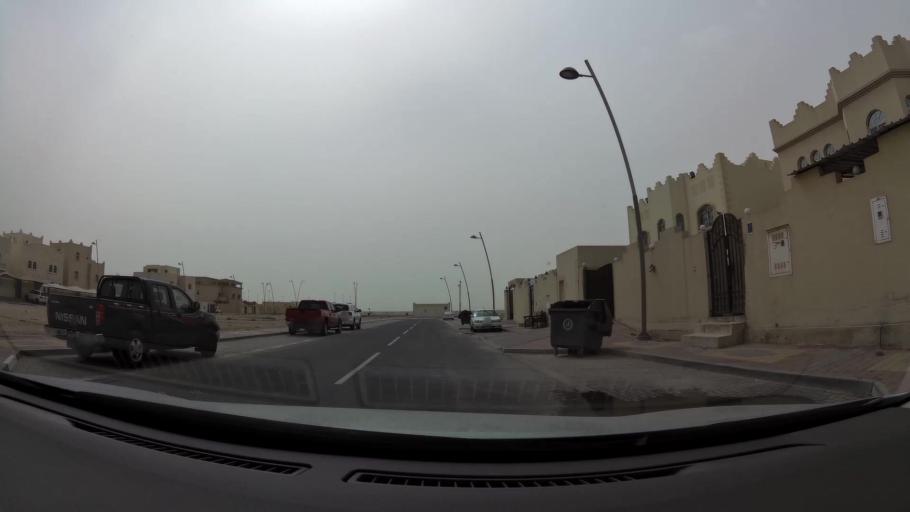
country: QA
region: Baladiyat ad Dawhah
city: Doha
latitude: 25.2256
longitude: 51.5376
